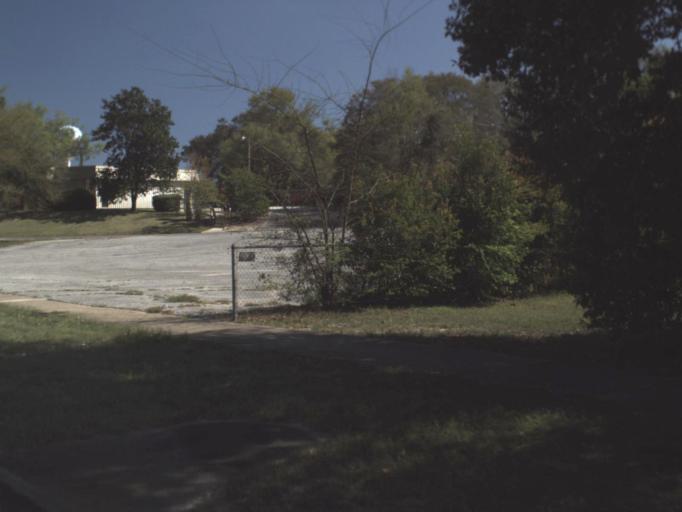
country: US
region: Florida
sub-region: Okaloosa County
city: Ocean City
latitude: 30.4236
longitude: -86.6154
